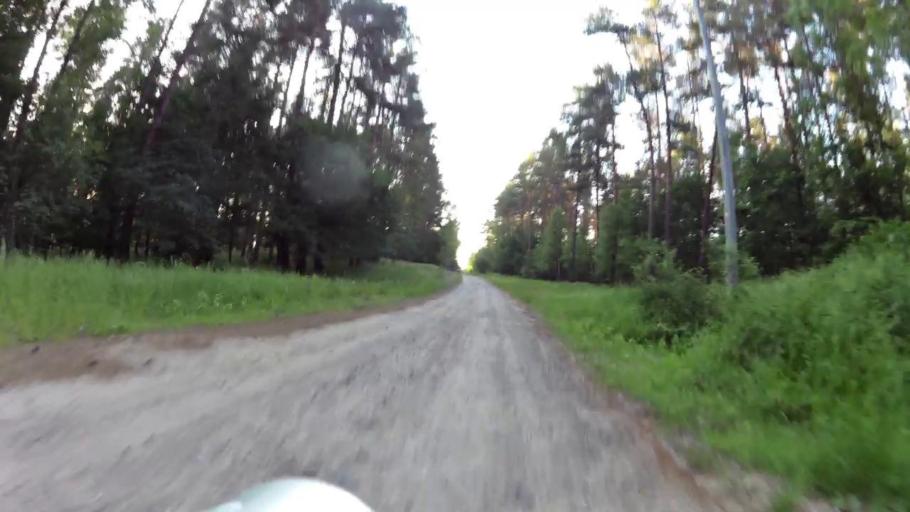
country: PL
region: West Pomeranian Voivodeship
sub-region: Powiat szczecinecki
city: Szczecinek
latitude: 53.8343
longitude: 16.6888
